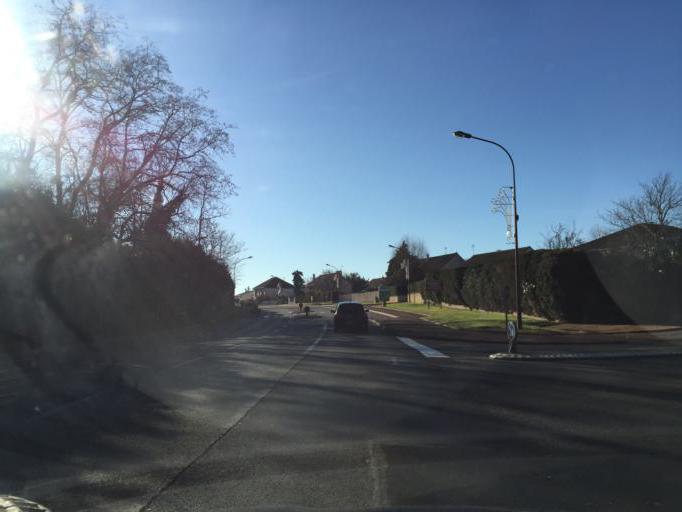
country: FR
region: Auvergne
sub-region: Departement de l'Allier
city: Saint-Remy-en-Rollat
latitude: 46.1636
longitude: 3.3937
